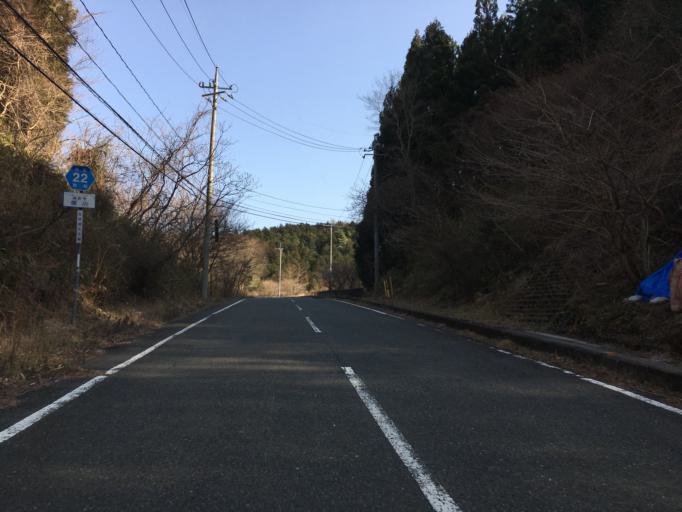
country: JP
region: Ibaraki
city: Kitaibaraki
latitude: 36.8064
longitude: 140.6287
